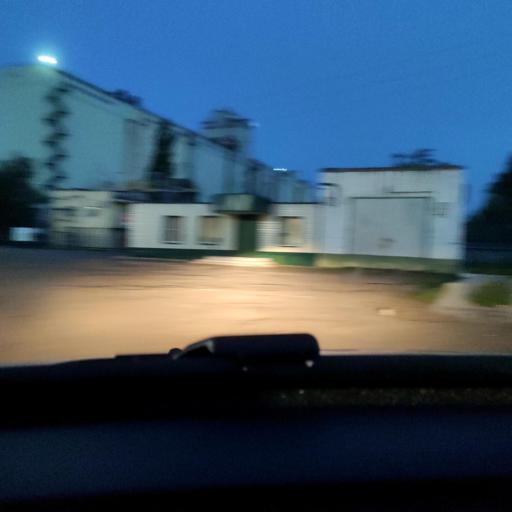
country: RU
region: Voronezj
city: Panino
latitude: 51.6442
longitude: 40.1273
